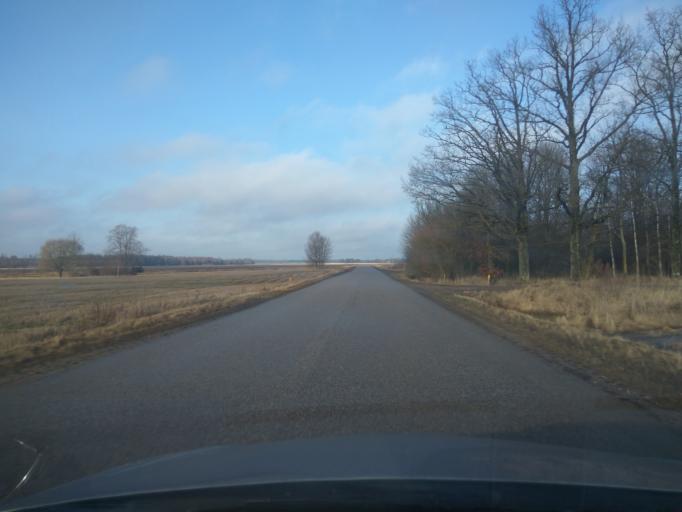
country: LV
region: Saldus Rajons
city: Saldus
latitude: 56.7994
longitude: 22.3814
